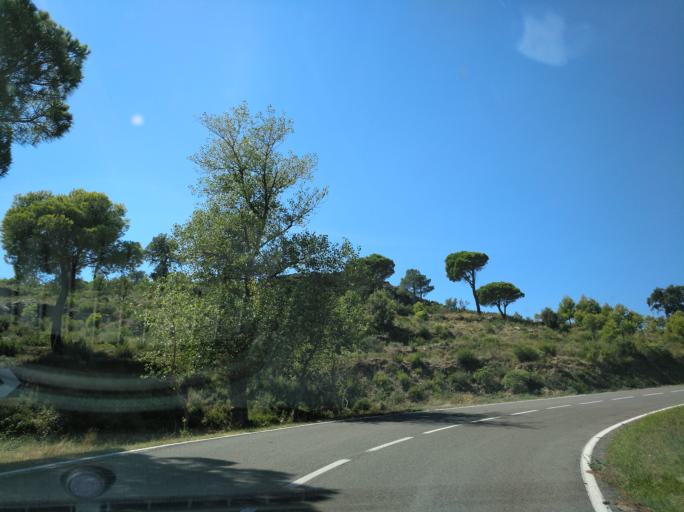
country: ES
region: Catalonia
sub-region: Provincia de Girona
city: Pau
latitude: 42.3314
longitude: 3.1316
